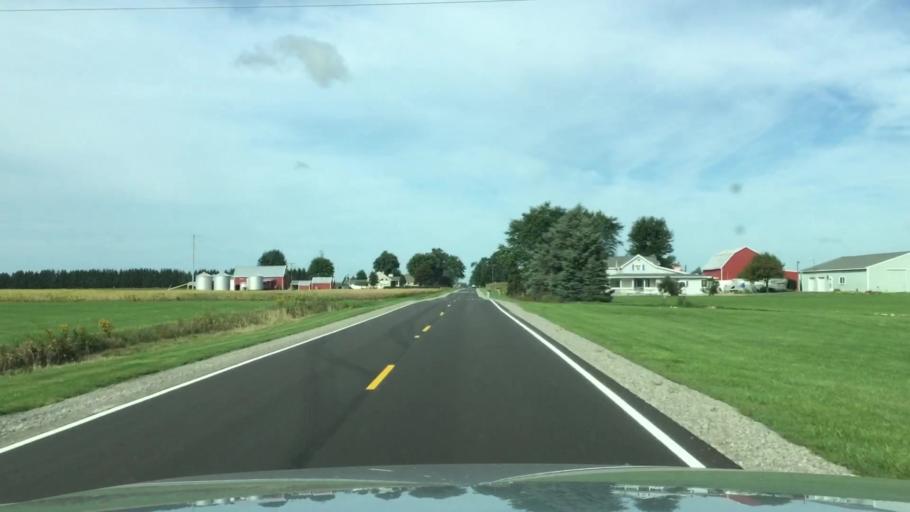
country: US
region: Michigan
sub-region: Genesee County
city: Montrose
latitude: 43.1471
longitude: -83.9433
